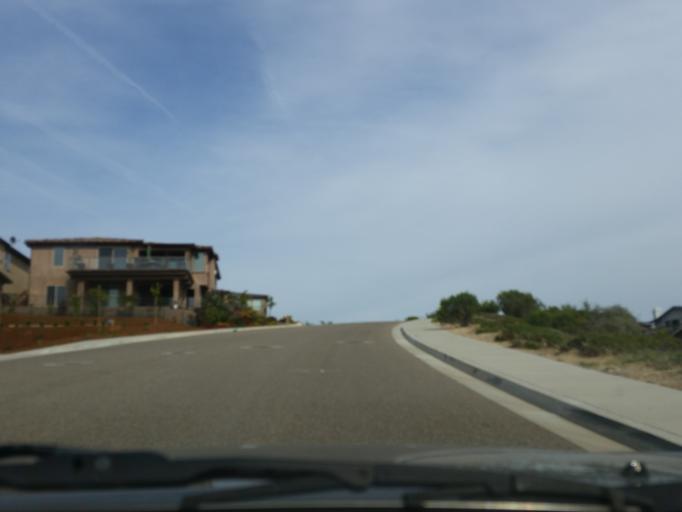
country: US
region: California
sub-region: San Luis Obispo County
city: Pismo Beach
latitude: 35.1444
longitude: -120.6271
